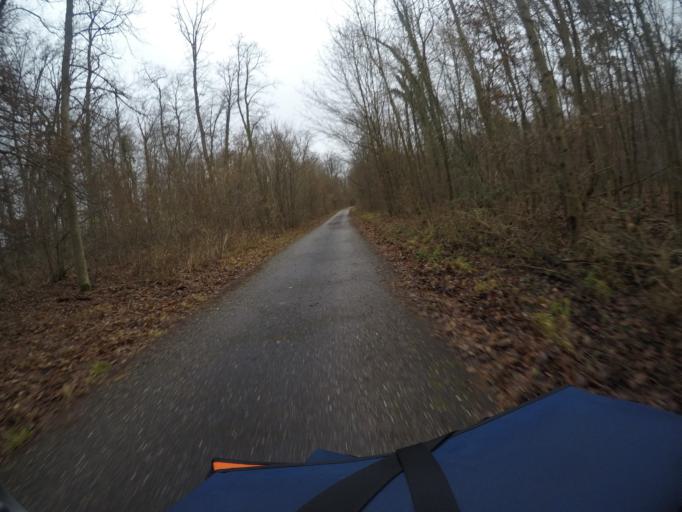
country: DE
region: Baden-Wuerttemberg
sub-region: Karlsruhe Region
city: Graben-Neudorf
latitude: 49.1942
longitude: 8.5035
